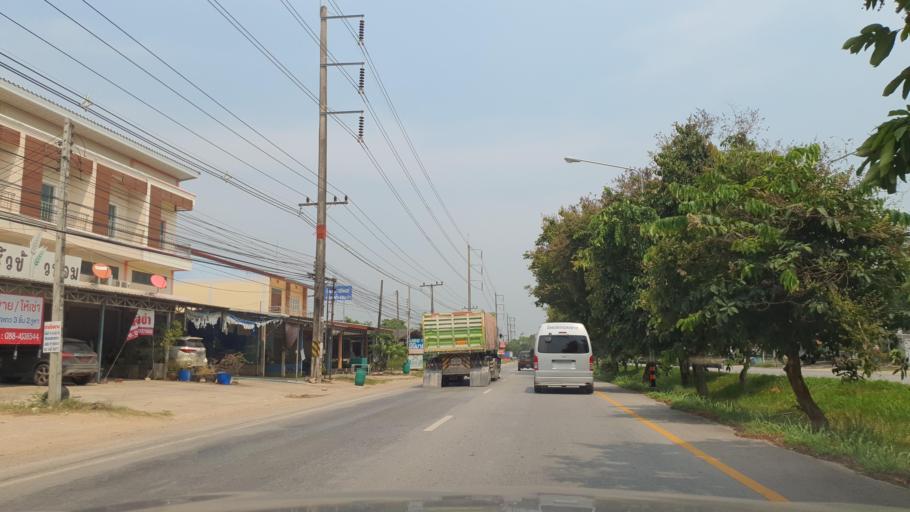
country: TH
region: Rayong
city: Rayong
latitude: 12.6411
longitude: 101.3600
